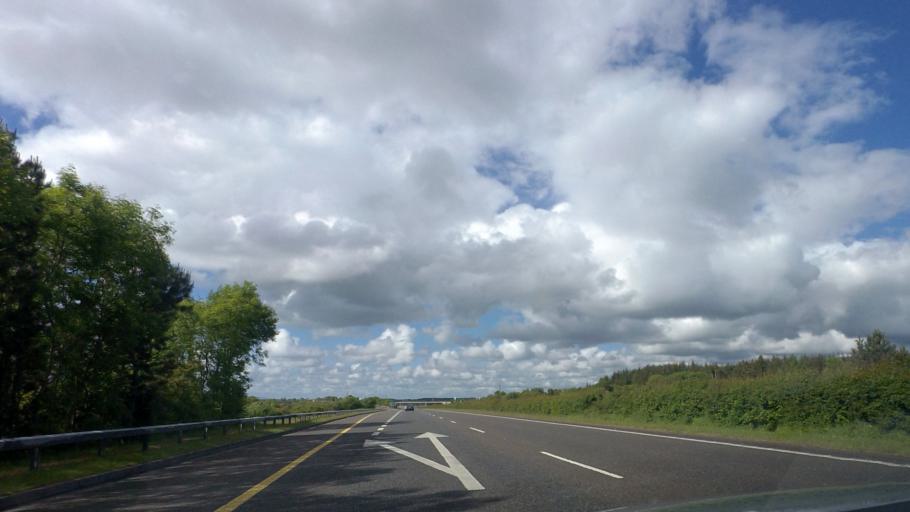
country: IE
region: Munster
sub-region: An Clar
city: Newmarket on Fergus
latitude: 52.7841
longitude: -8.9217
